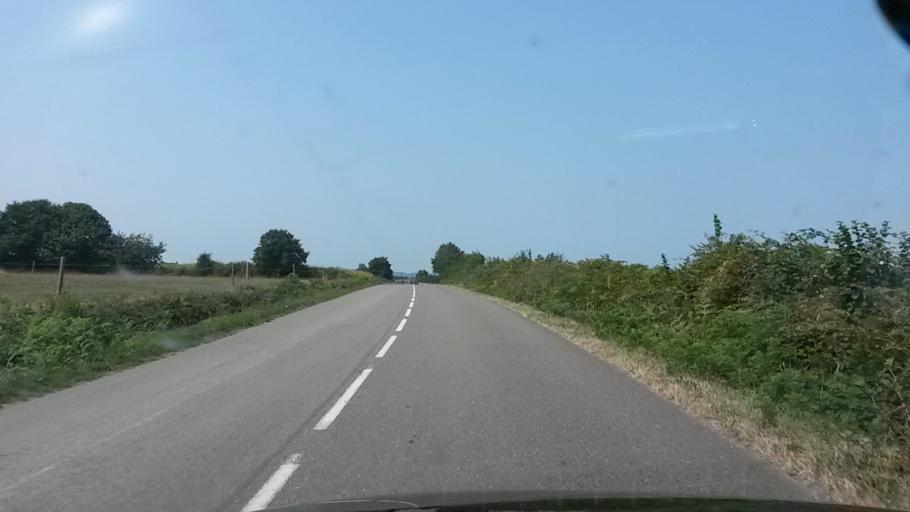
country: FR
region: Pays de la Loire
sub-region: Departement de la Mayenne
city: Villaines-la-Juhel
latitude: 48.3589
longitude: -0.2226
